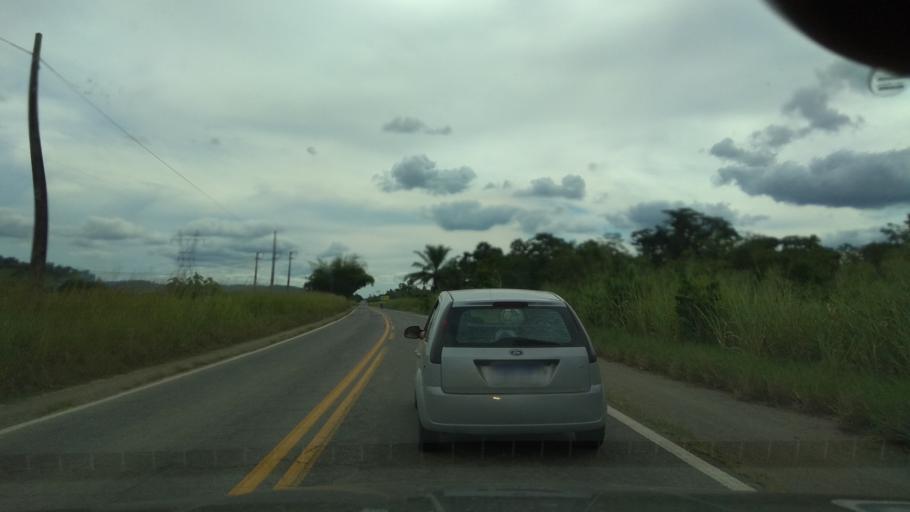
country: BR
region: Bahia
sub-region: Ipiau
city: Ipiau
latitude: -14.1479
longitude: -39.7029
